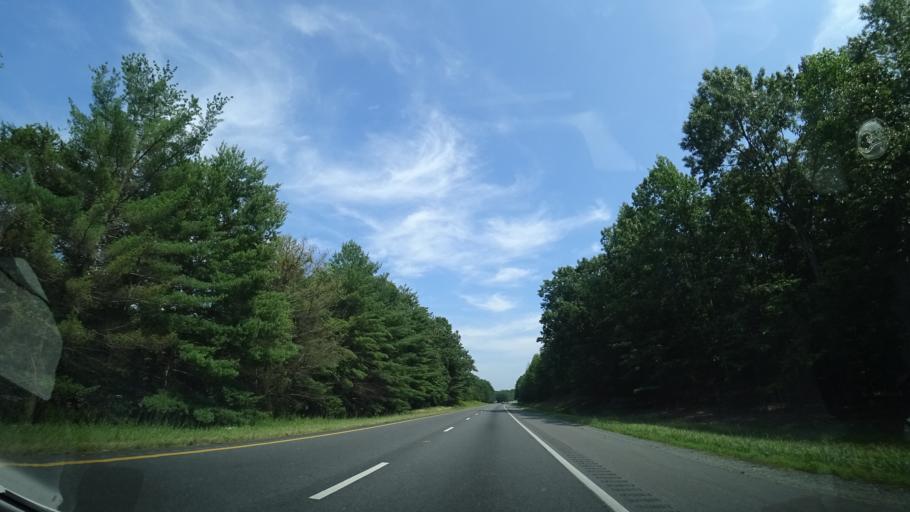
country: US
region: Virginia
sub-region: Louisa County
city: Louisa
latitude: 37.9028
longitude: -78.0525
